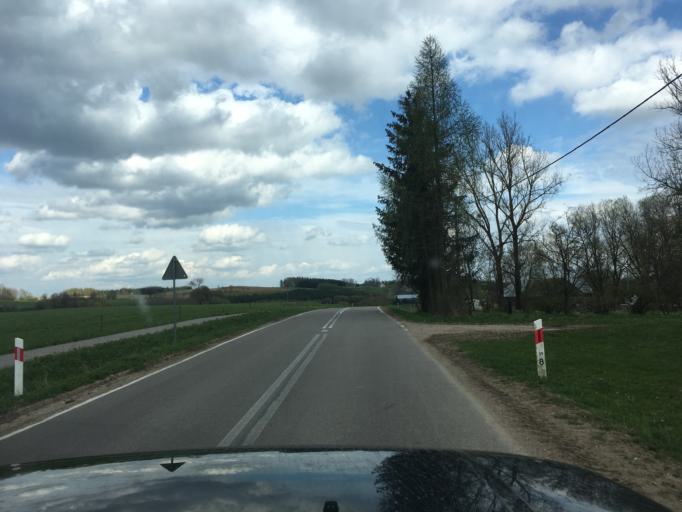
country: PL
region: Podlasie
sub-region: Powiat suwalski
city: Filipow
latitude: 54.3612
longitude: 22.7991
